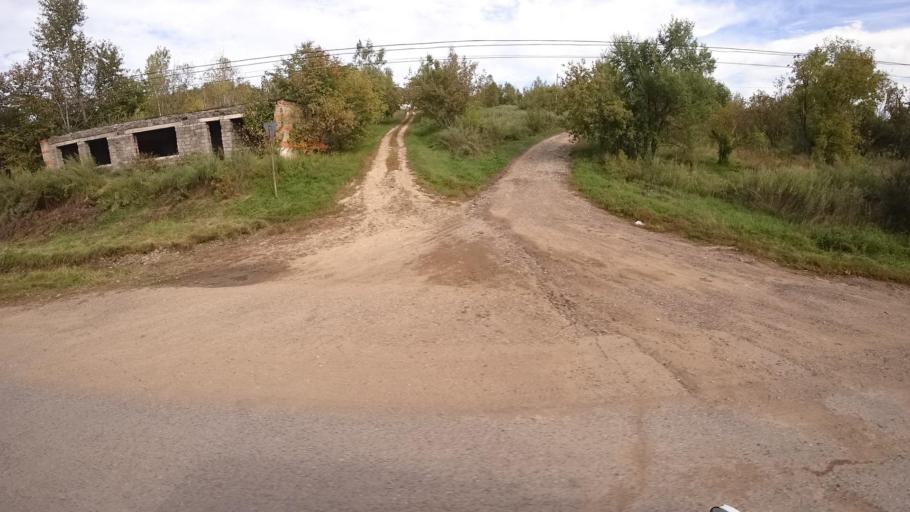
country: RU
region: Primorskiy
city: Dostoyevka
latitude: 44.3263
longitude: 133.4769
